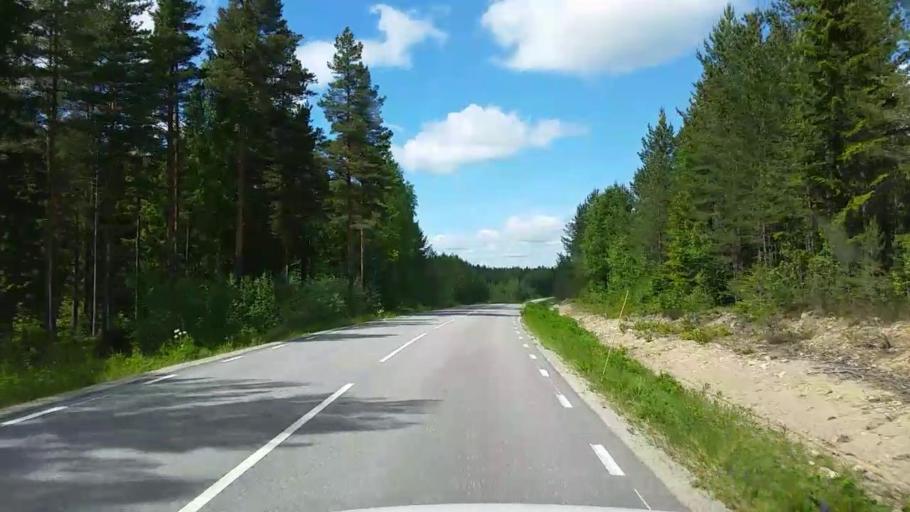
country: SE
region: Gaevleborg
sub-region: Ovanakers Kommun
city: Alfta
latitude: 61.2752
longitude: 16.1101
